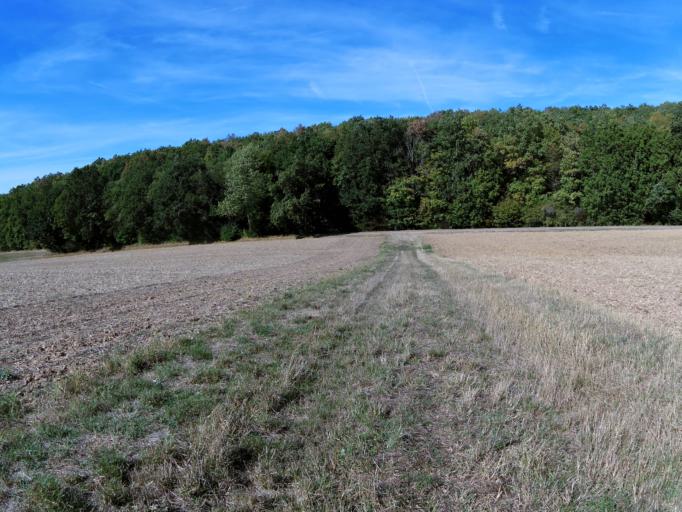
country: DE
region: Bavaria
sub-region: Regierungsbezirk Unterfranken
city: Eisingen
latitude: 49.7696
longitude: 9.8221
